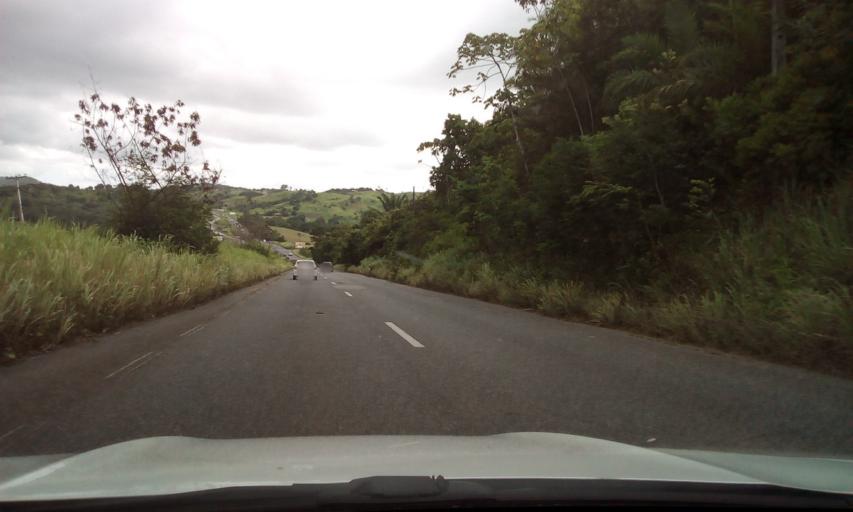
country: BR
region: Pernambuco
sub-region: Moreno
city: Moreno
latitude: -8.1116
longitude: -35.1419
